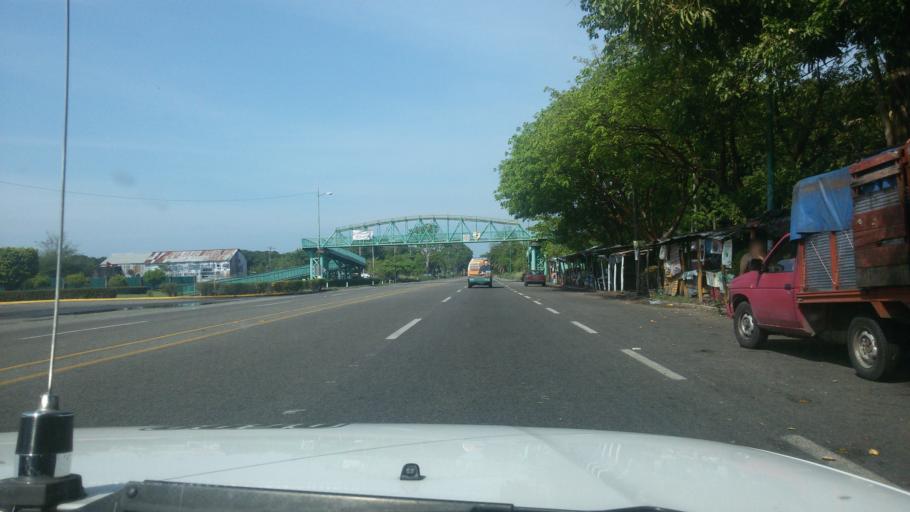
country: MX
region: Chiapas
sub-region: Tapachula
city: Congregacion Reforma
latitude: 14.8106
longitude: -92.3466
